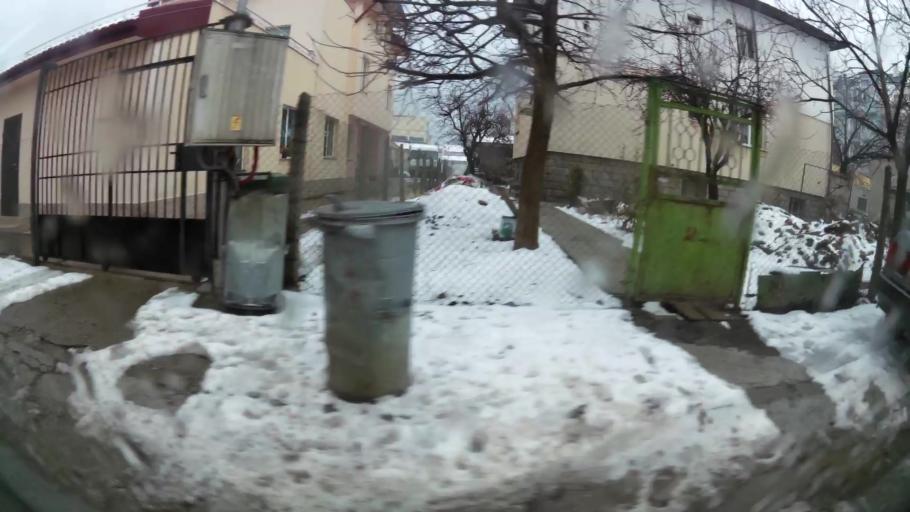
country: BG
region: Sofia-Capital
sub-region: Stolichna Obshtina
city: Sofia
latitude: 42.6790
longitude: 23.2592
